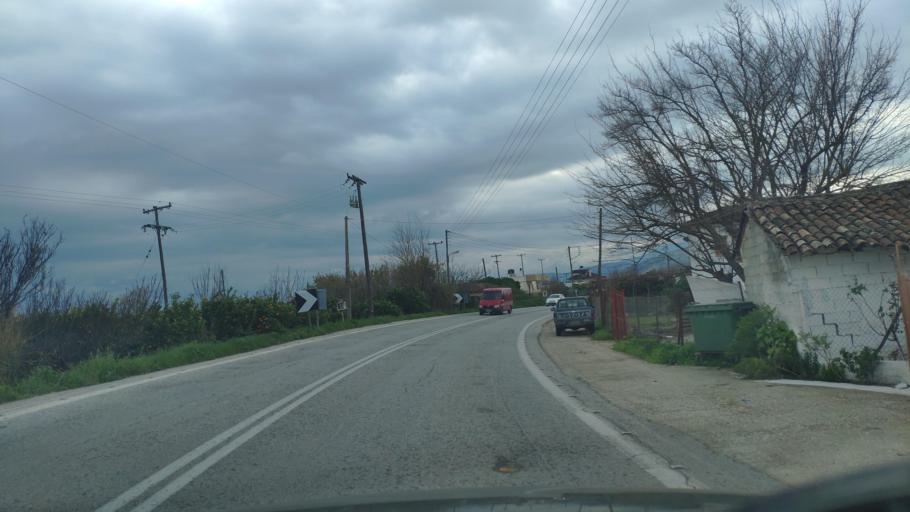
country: GR
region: Peloponnese
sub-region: Nomos Argolidos
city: Nea Kios
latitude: 37.5854
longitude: 22.7096
